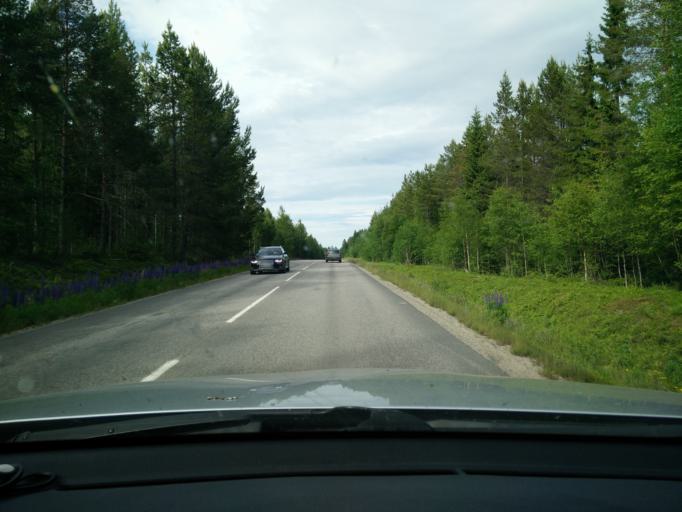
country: SE
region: Gaevleborg
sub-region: Nordanstigs Kommun
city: Bergsjoe
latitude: 61.9296
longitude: 17.0321
